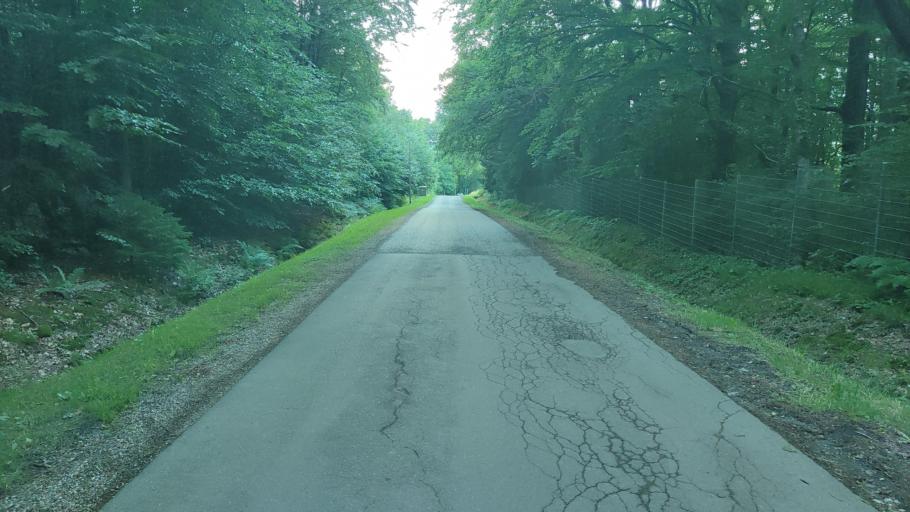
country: DE
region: North Rhine-Westphalia
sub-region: Regierungsbezirk Koln
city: Roetgen
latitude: 50.6303
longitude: 6.1841
